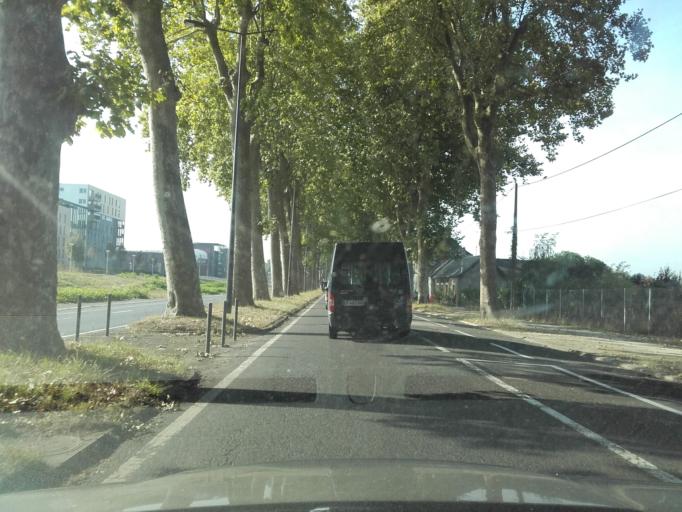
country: FR
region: Centre
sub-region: Departement d'Indre-et-Loire
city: Tours
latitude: 47.3695
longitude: 0.6768
